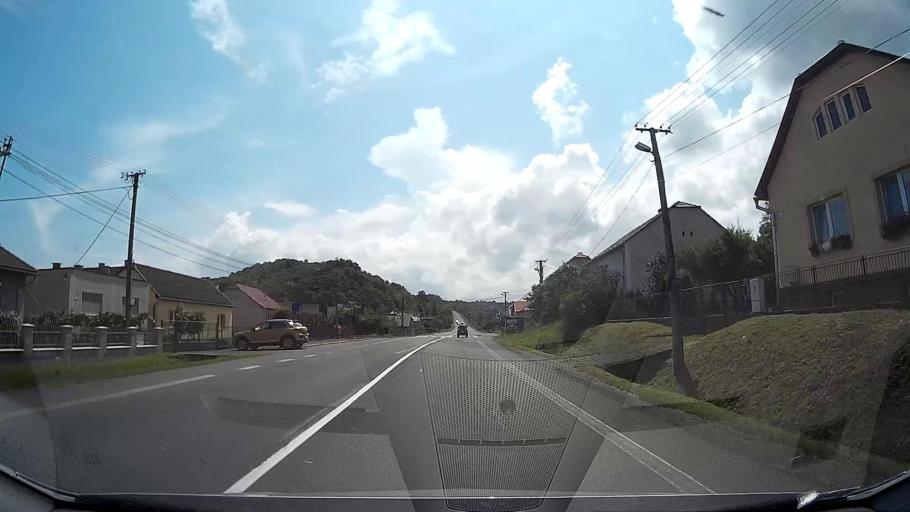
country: SK
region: Banskobystricky
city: Fil'akovo
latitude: 48.2868
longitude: 19.7956
